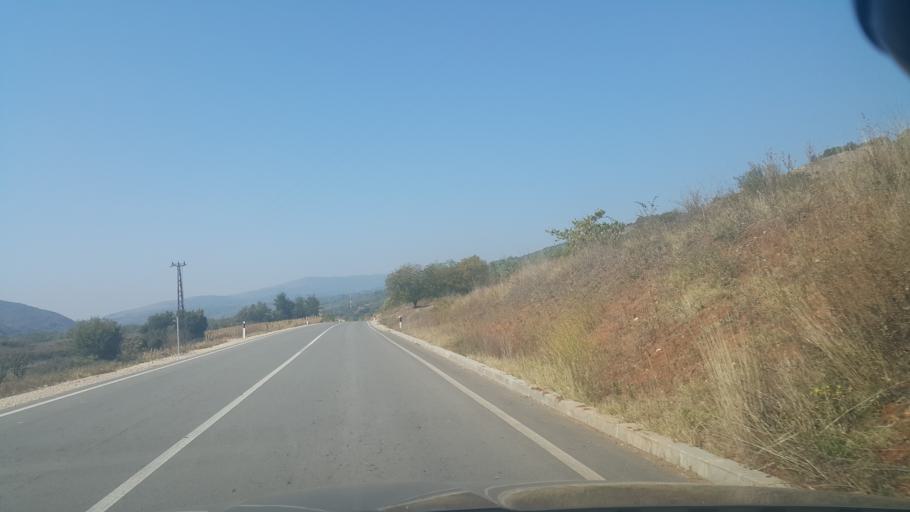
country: RS
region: Central Serbia
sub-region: Pirotski Okrug
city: Pirot
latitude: 43.2155
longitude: 22.5063
